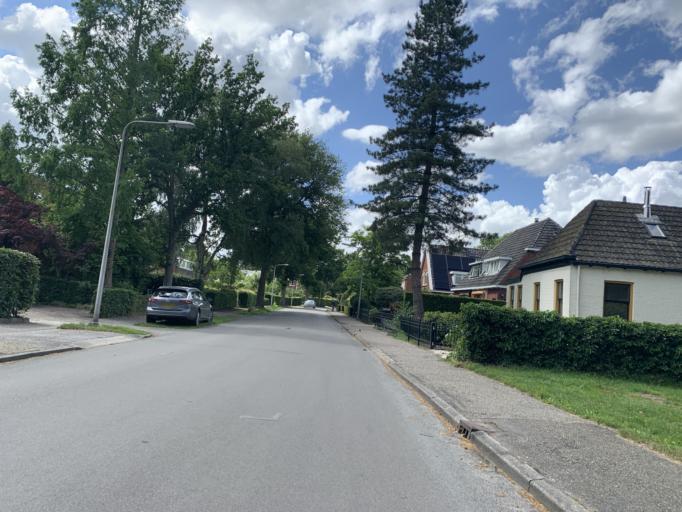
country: NL
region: Groningen
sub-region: Gemeente Haren
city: Haren
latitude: 53.1651
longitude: 6.6239
